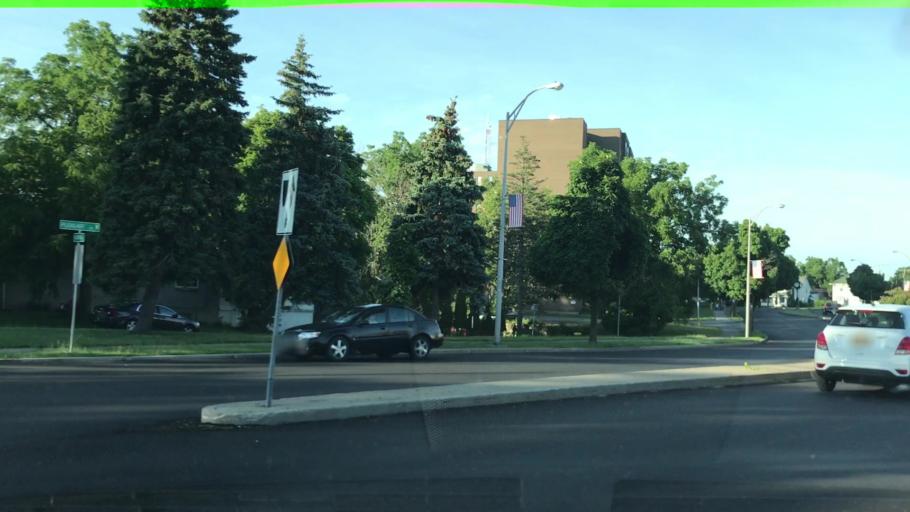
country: US
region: New York
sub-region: Erie County
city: Lancaster
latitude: 42.9021
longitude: -78.6729
